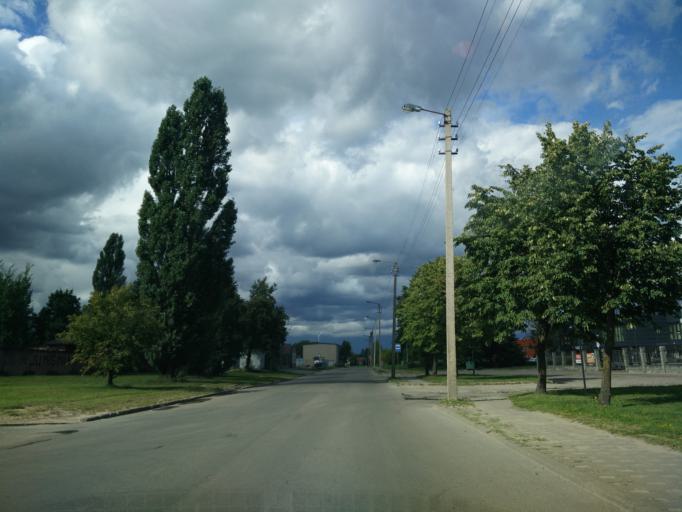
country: LT
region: Kauno apskritis
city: Dainava (Kaunas)
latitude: 54.9090
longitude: 24.0097
